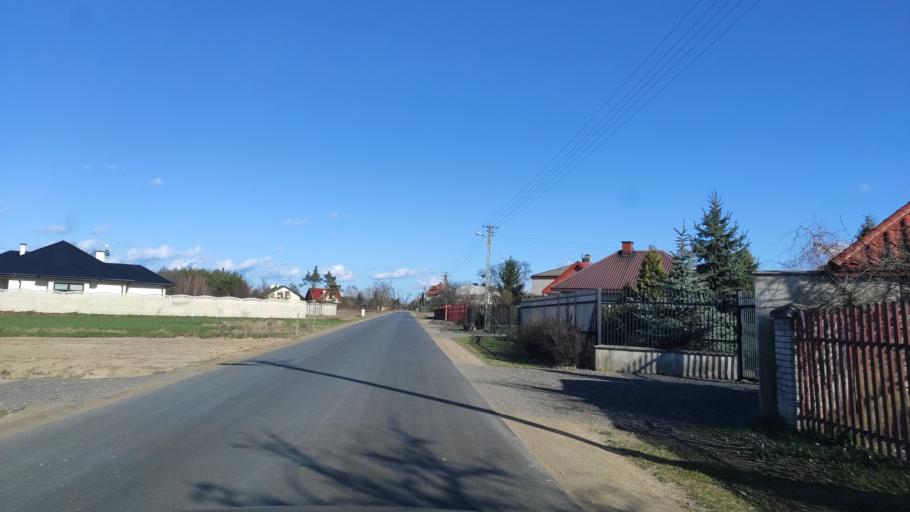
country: PL
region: Masovian Voivodeship
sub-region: Powiat radomski
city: Jastrzebia
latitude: 51.4533
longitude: 21.2499
